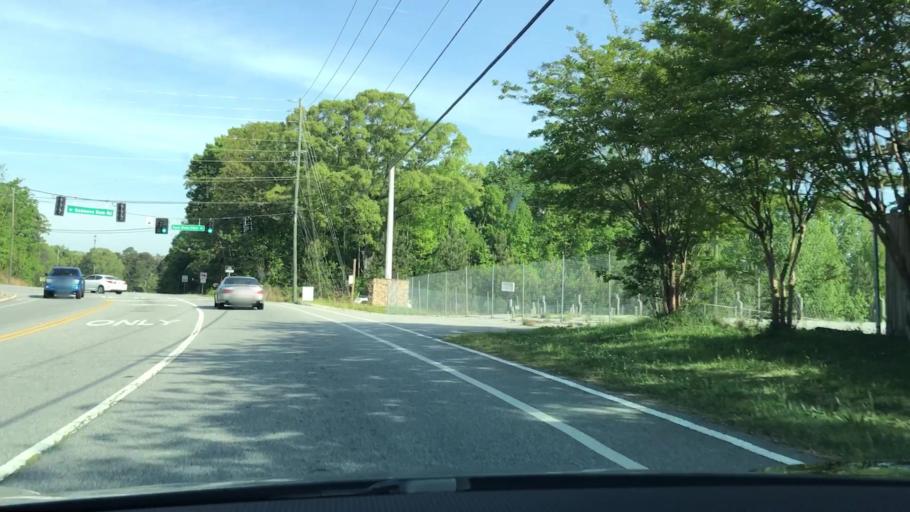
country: US
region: Georgia
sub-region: Gwinnett County
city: Sugar Hill
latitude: 34.1472
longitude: -84.0611
